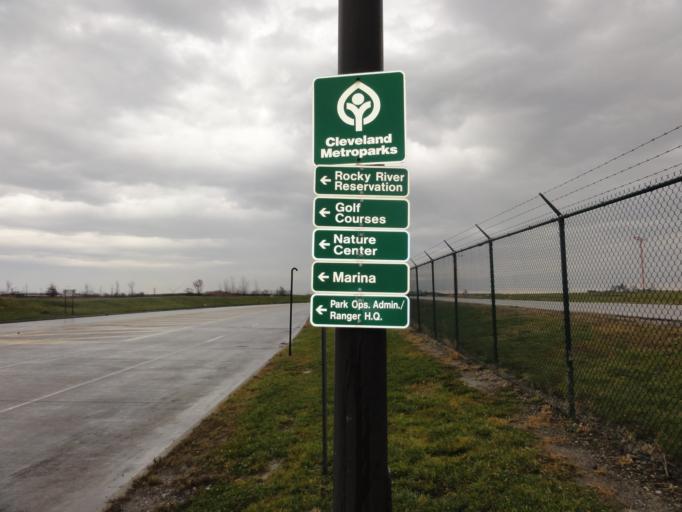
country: US
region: Ohio
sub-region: Cuyahoga County
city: Fairview Park
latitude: 41.4203
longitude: -81.8439
